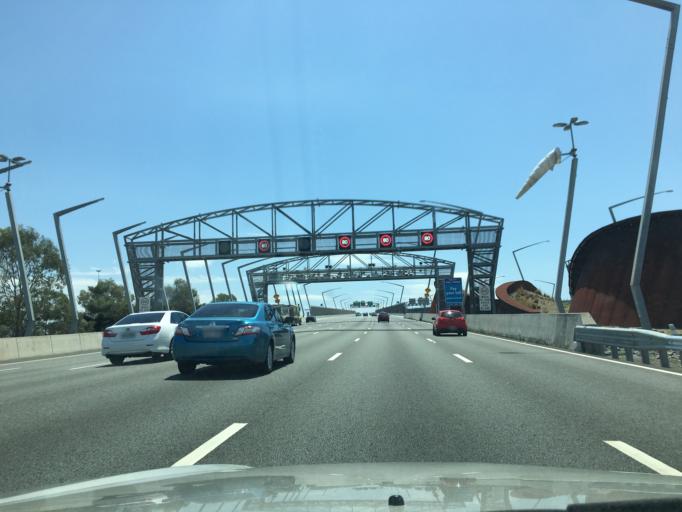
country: AU
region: Queensland
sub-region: Brisbane
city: Cannon Hill
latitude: -27.4519
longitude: 153.1046
